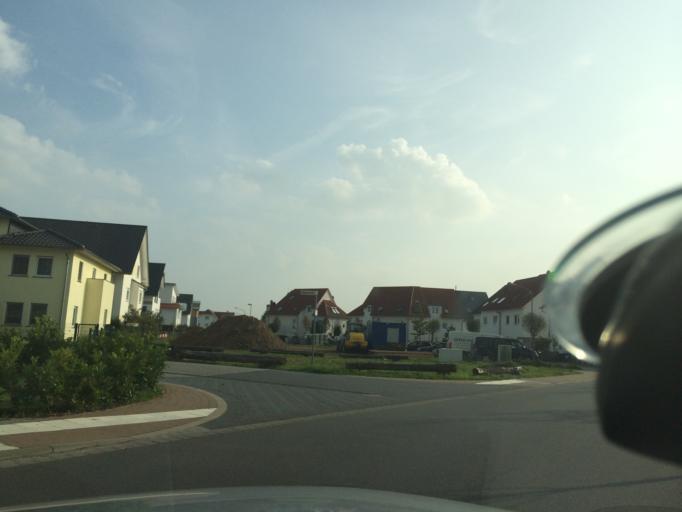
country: DE
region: Hesse
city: Griesheim
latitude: 49.8697
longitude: 8.5665
